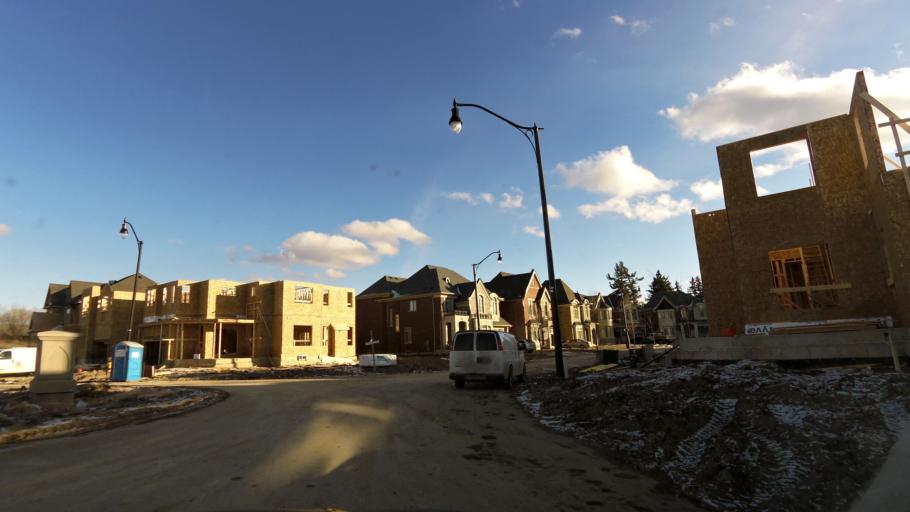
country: CA
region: Ontario
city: Brampton
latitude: 43.6492
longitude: -79.7766
